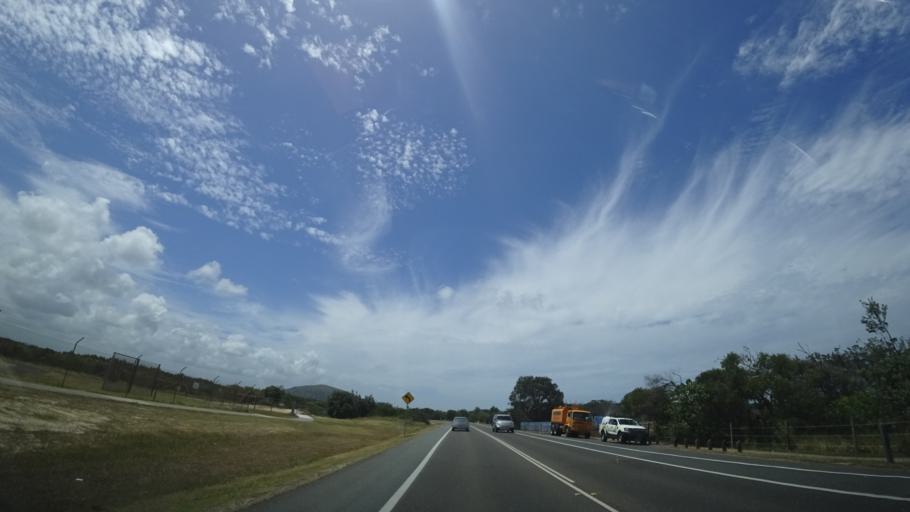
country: AU
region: Queensland
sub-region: Sunshine Coast
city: Coolum Beach
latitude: -26.5922
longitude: 153.0965
